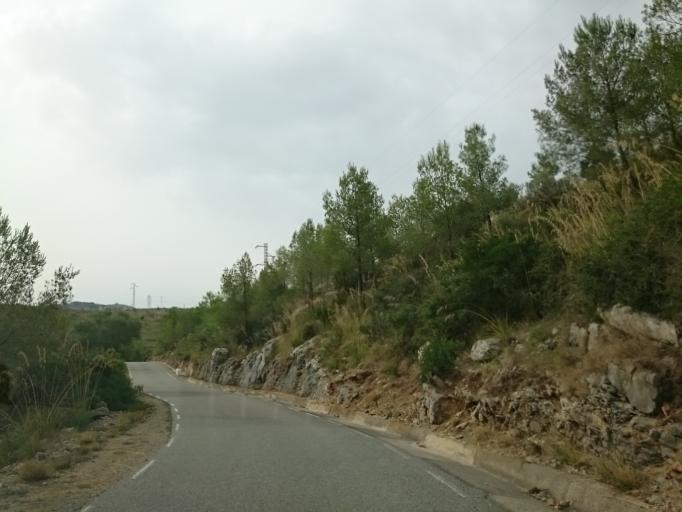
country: ES
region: Catalonia
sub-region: Provincia de Barcelona
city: Olivella
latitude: 41.3034
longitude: 1.8457
